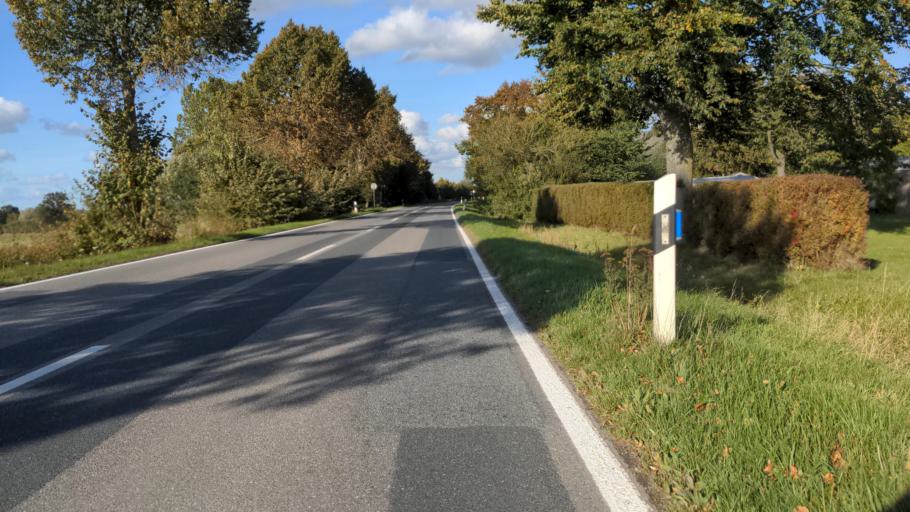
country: DE
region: Schleswig-Holstein
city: Beschendorf
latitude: 54.1728
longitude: 10.8744
